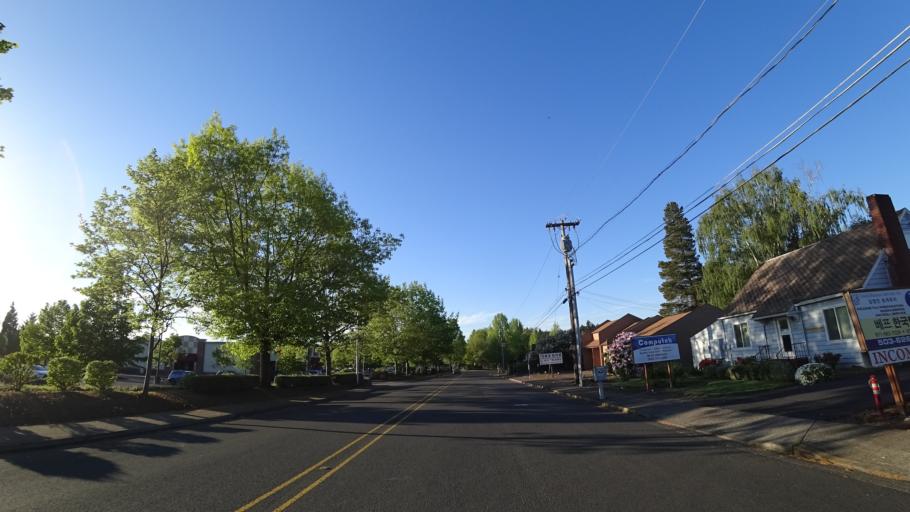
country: US
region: Oregon
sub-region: Washington County
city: Beaverton
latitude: 45.4893
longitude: -122.7901
